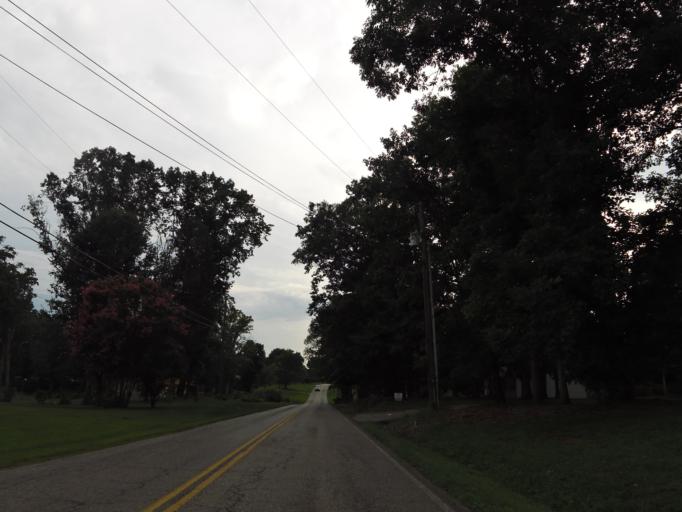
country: US
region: Tennessee
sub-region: Loudon County
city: Greenback
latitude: 35.6982
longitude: -84.0819
